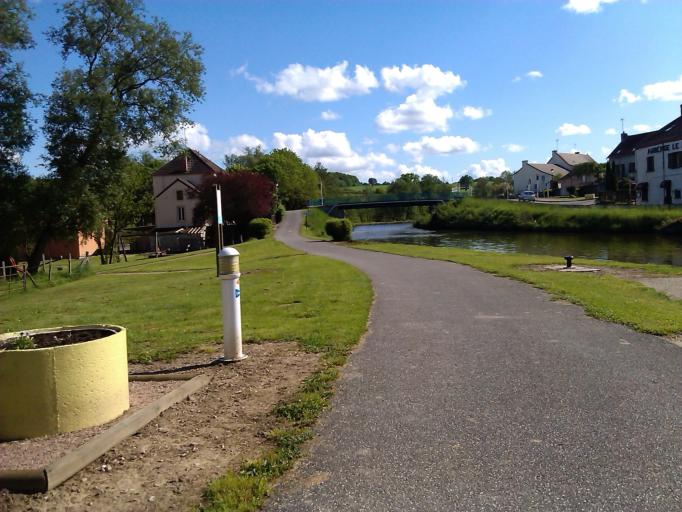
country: FR
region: Bourgogne
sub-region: Departement de Saone-et-Loire
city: Ecuisses
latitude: 46.7742
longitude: 4.5438
